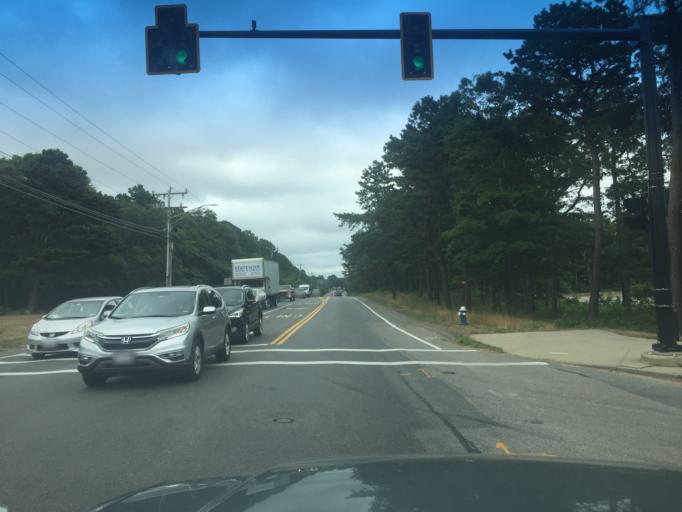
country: US
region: Massachusetts
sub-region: Barnstable County
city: Mashpee
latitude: 41.6179
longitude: -70.4948
